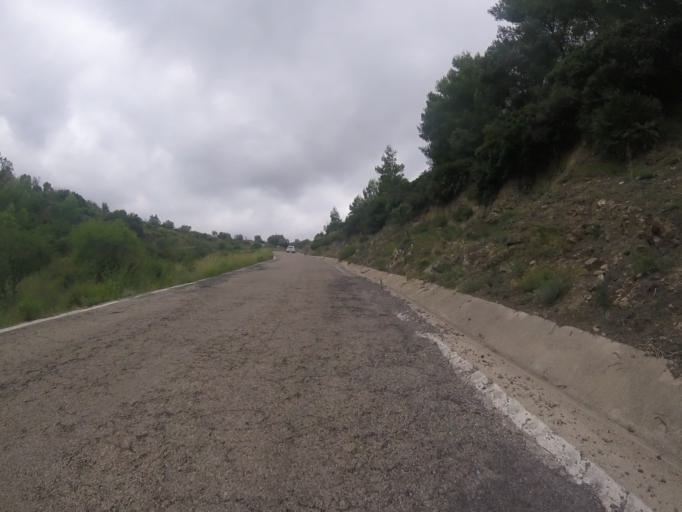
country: ES
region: Valencia
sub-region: Provincia de Castello
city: Cabanes
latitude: 40.1211
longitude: 0.0459
